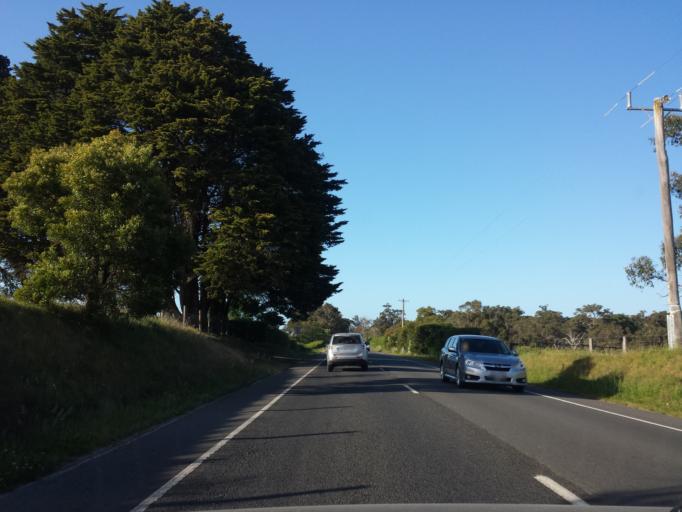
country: AU
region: Victoria
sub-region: Casey
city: Narre Warren North
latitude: -37.9854
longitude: 145.3529
